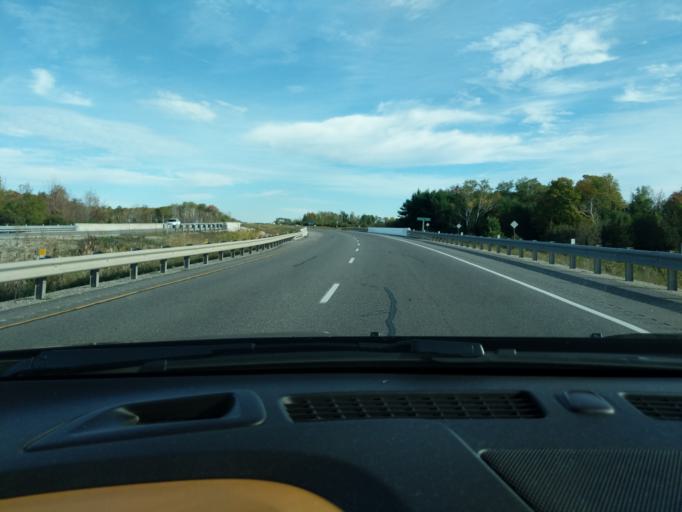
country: CA
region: Ontario
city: Collingwood
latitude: 44.4825
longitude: -80.1706
